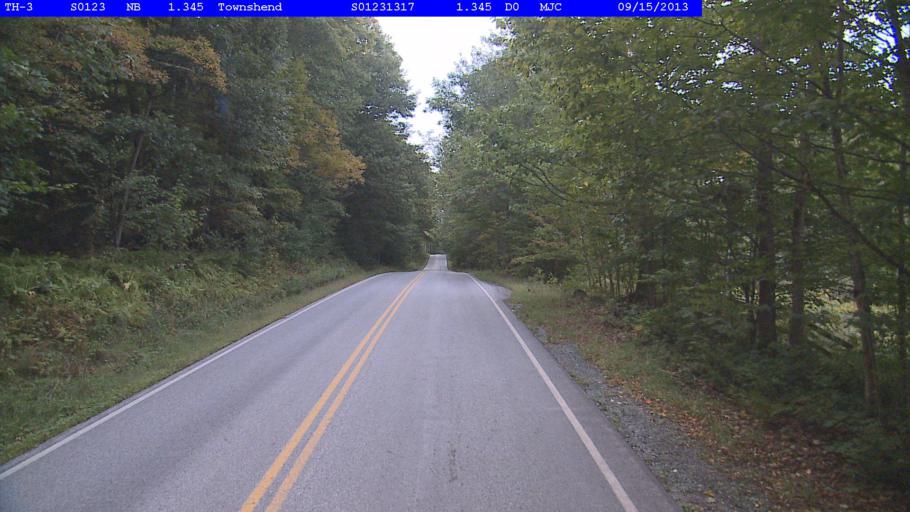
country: US
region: Vermont
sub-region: Windham County
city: Newfane
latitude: 43.1021
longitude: -72.7093
